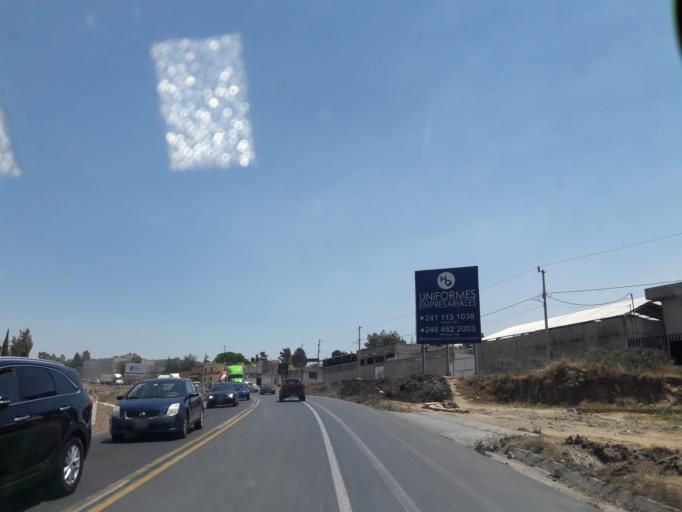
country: MX
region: Tlaxcala
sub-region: Apetatitlan de Antonio Carvajal
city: Belen Atzitzimititlan
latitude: 19.3483
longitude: -98.1930
